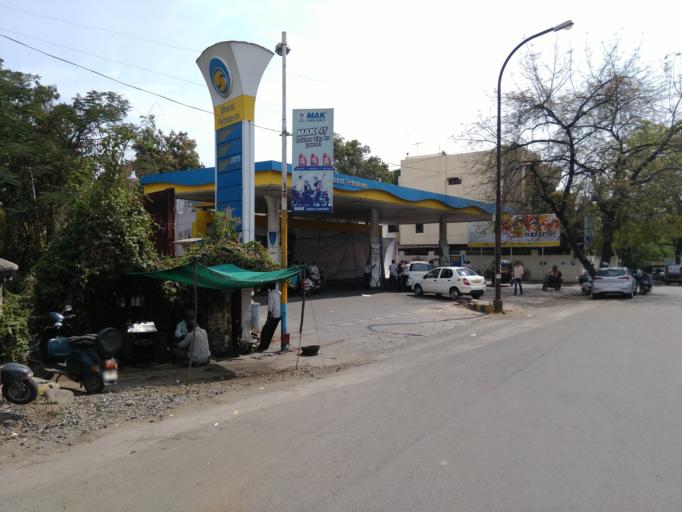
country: IN
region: Maharashtra
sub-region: Nagpur Division
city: Nagpur
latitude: 21.1718
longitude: 79.0799
